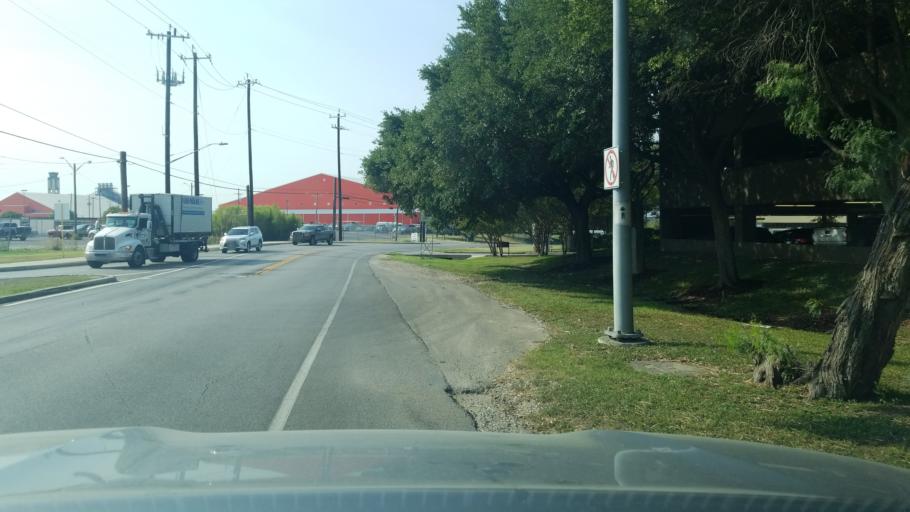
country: US
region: Texas
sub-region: Bexar County
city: Castle Hills
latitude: 29.5323
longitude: -98.4833
